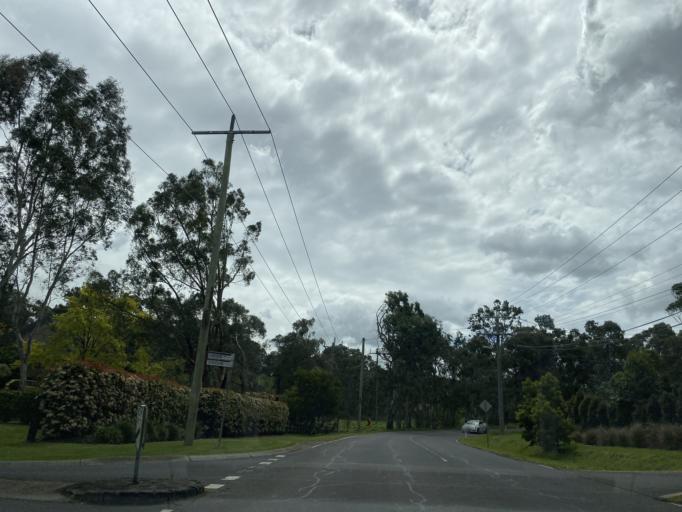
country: AU
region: Victoria
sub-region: Banyule
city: Lower Plenty
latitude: -37.7369
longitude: 145.1157
